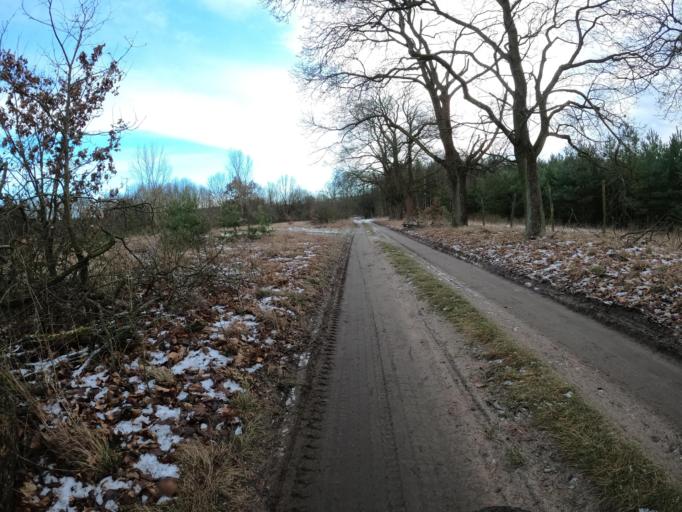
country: PL
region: Lubusz
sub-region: Powiat slubicki
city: Cybinka
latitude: 52.2077
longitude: 14.8480
